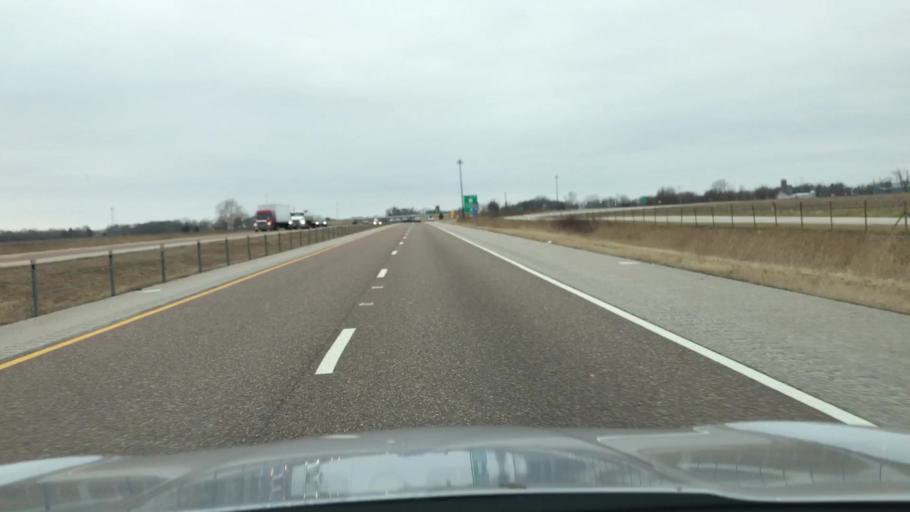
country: US
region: Illinois
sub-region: Madison County
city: Worden
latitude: 38.9340
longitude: -89.7974
